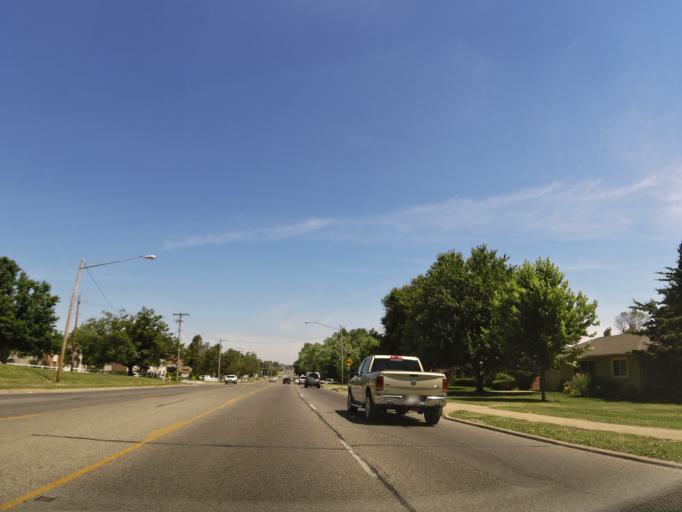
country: US
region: Illinois
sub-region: Vermilion County
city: Danville
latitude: 40.1607
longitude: -87.6304
